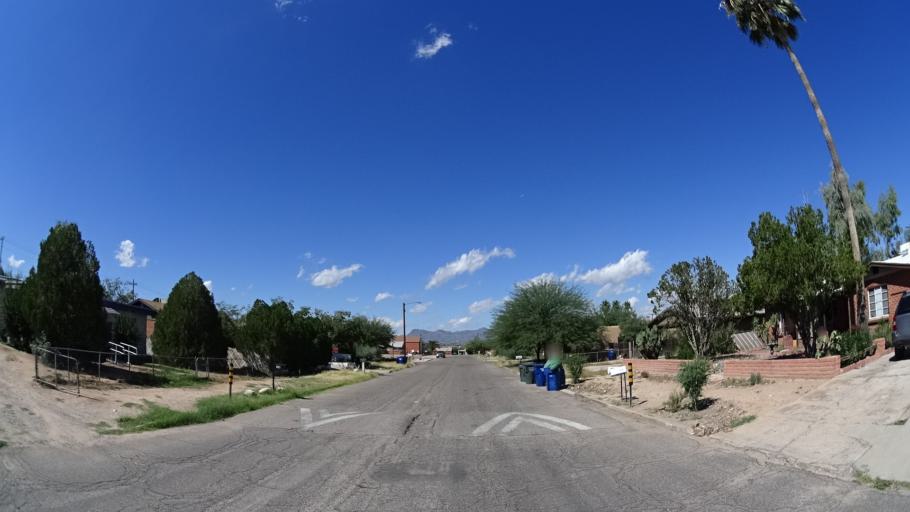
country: US
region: Arizona
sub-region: Pima County
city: South Tucson
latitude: 32.2436
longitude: -110.9665
